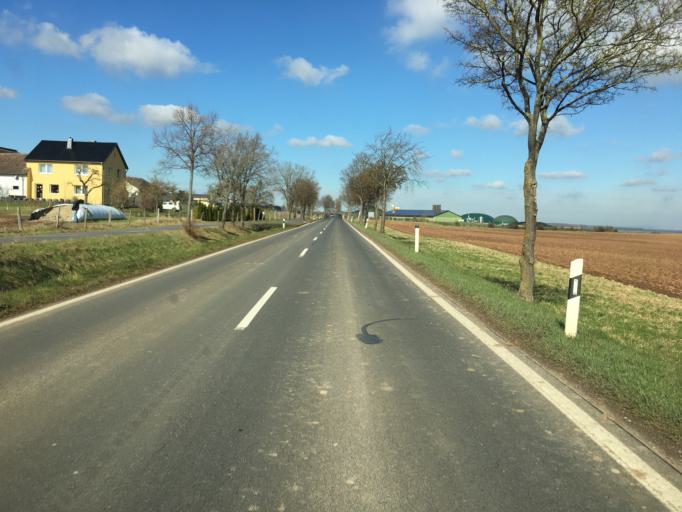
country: DE
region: North Rhine-Westphalia
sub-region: Regierungsbezirk Koln
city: Mechernich
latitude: 50.6161
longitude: 6.6435
